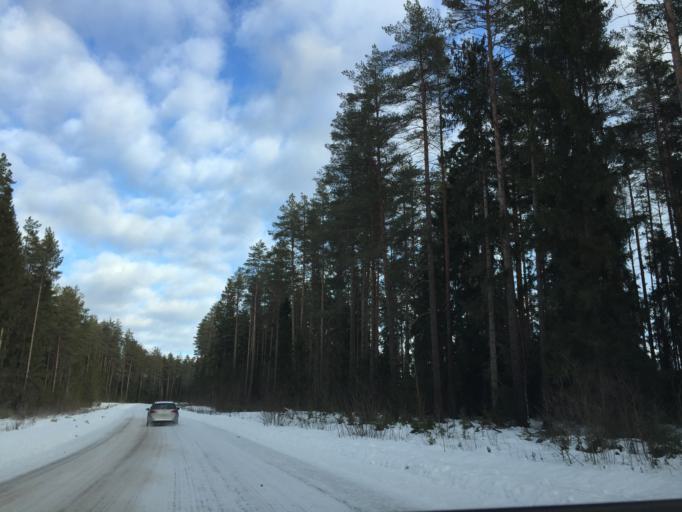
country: LV
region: Ogre
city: Jumprava
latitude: 56.5572
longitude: 24.9019
